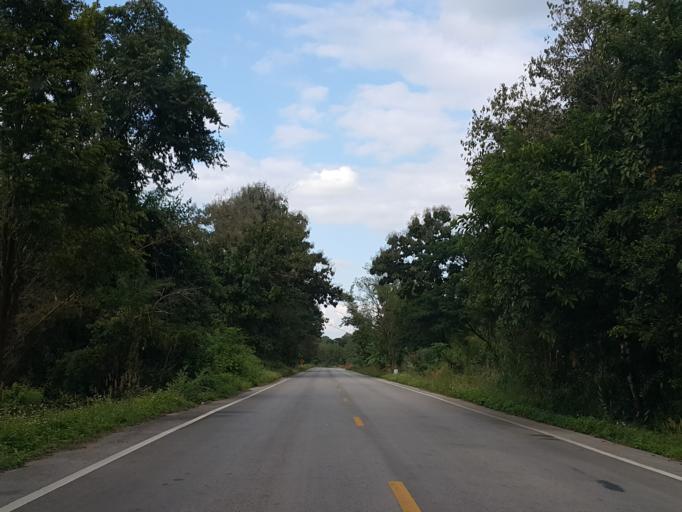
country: TH
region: Lampang
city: Chae Hom
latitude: 18.6390
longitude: 99.4936
